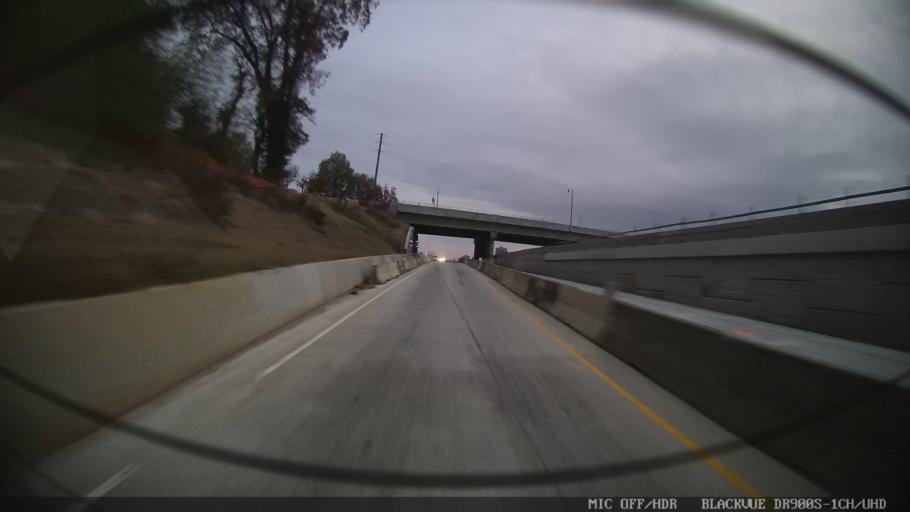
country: US
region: Georgia
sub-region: Fulton County
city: Sandy Springs
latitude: 33.9310
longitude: -84.3573
